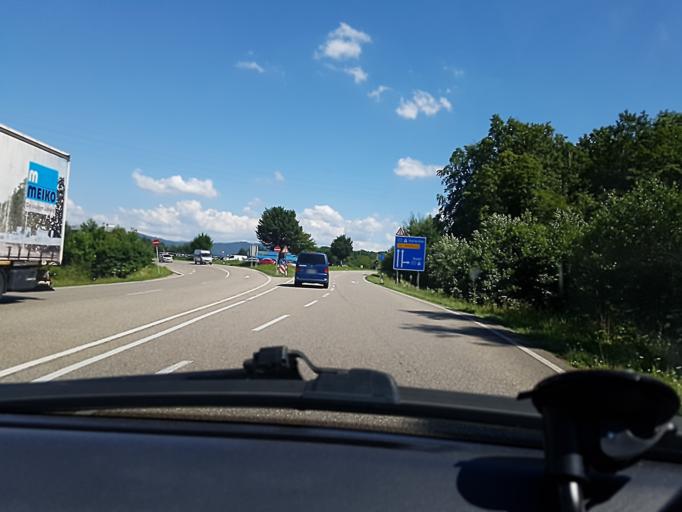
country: DE
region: Baden-Wuerttemberg
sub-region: Freiburg Region
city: Schutterwald
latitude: 48.4730
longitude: 7.8996
